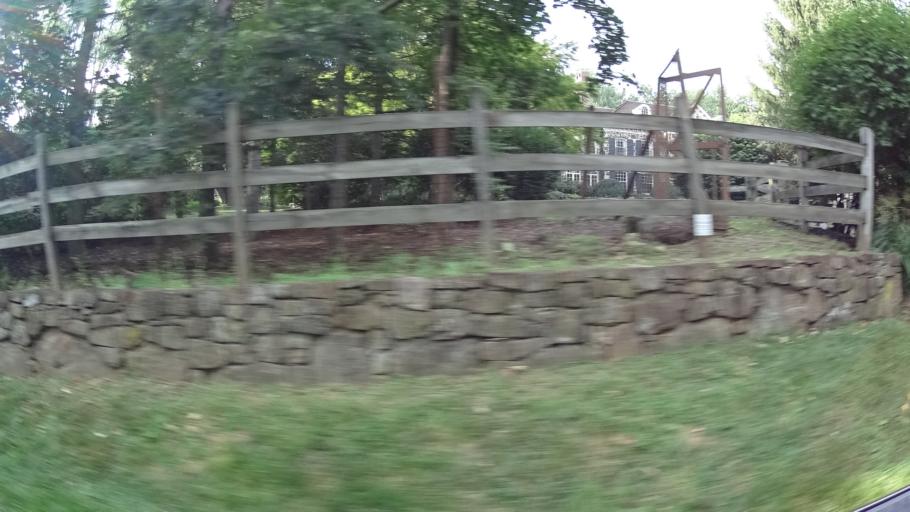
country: US
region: New Jersey
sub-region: Morris County
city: Morristown
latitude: 40.7336
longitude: -74.4857
